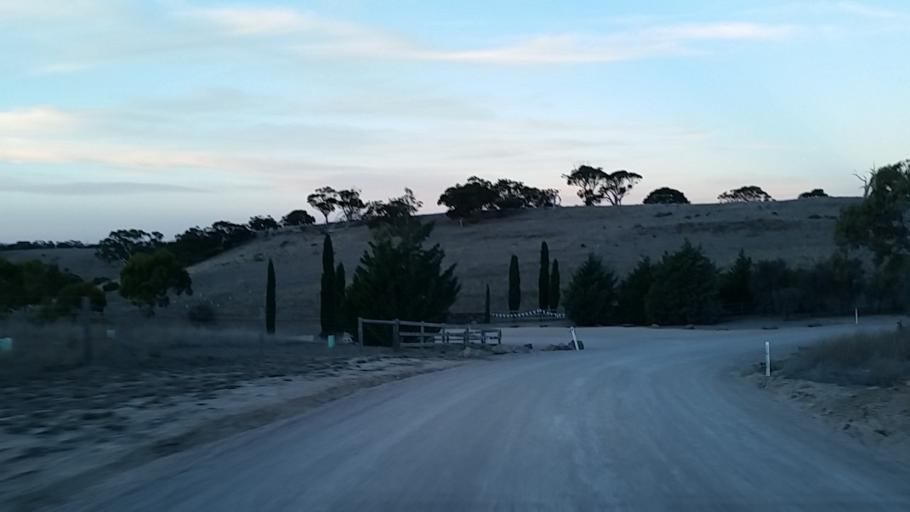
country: AU
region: South Australia
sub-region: Mount Barker
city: Nairne
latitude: -35.0905
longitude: 138.9501
